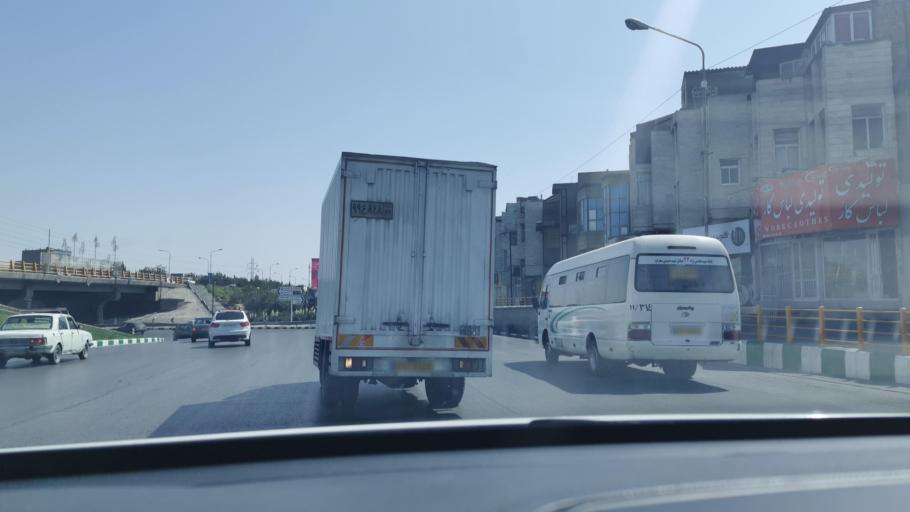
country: IR
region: Razavi Khorasan
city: Mashhad
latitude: 36.3105
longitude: 59.6541
